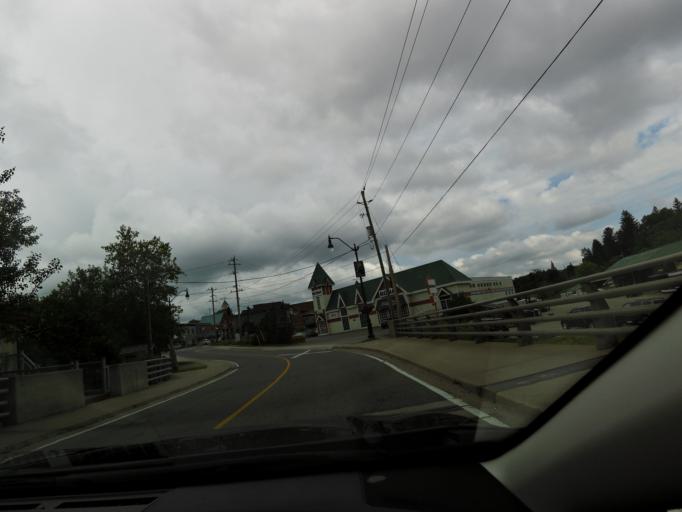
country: CA
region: Ontario
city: Bracebridge
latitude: 45.0401
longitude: -79.3071
